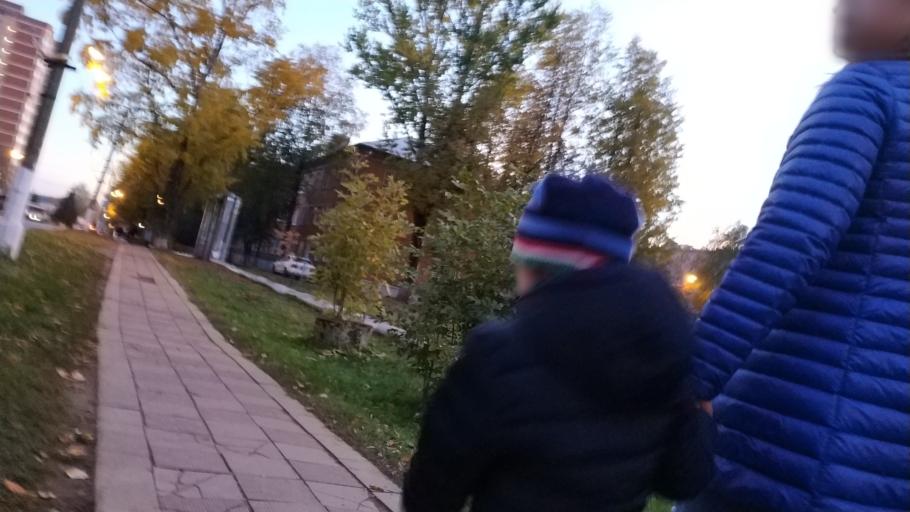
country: RU
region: Moskovskaya
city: Lobnya
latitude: 56.0202
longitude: 37.4221
